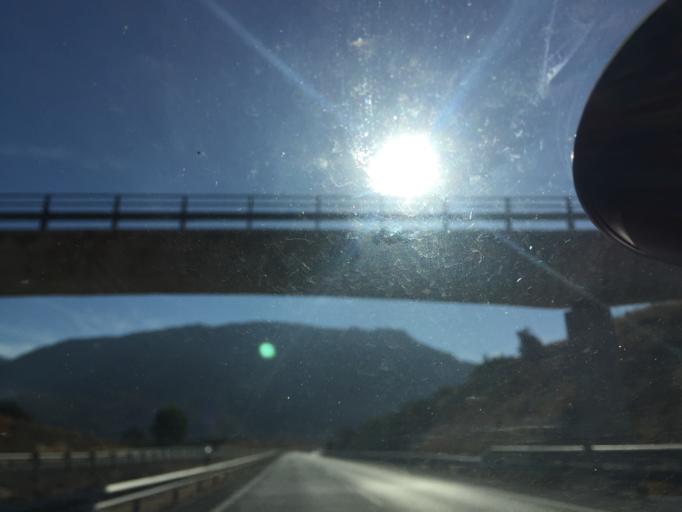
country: ES
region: Andalusia
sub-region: Provincia de Jaen
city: La Guardia de Jaen
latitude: 37.7513
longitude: -3.6940
